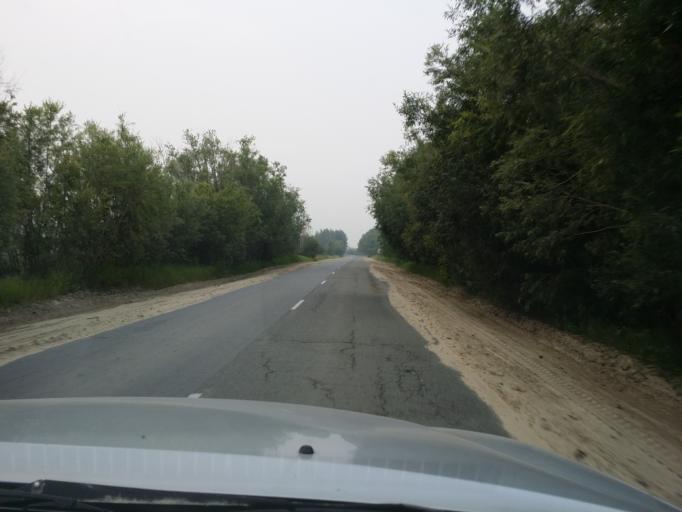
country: RU
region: Khanty-Mansiyskiy Avtonomnyy Okrug
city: Megion
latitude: 61.0108
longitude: 76.3127
